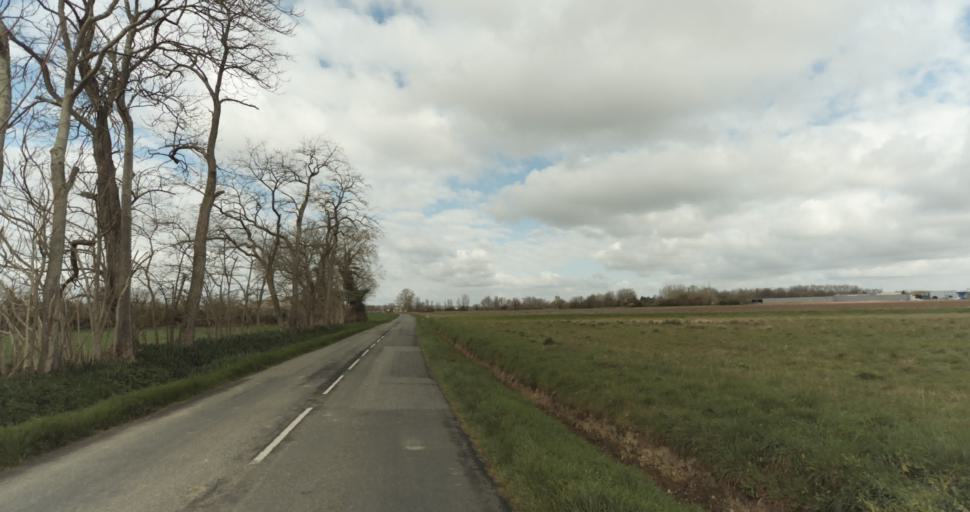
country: FR
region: Midi-Pyrenees
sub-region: Departement de la Haute-Garonne
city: Auterive
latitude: 43.3581
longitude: 1.4518
